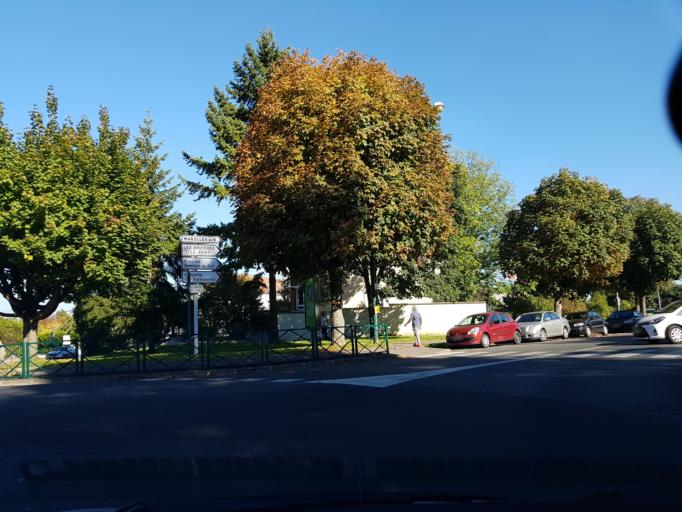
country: FR
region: Ile-de-France
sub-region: Departement du Val-de-Marne
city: Sucy-en-Brie
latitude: 48.7717
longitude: 2.5274
